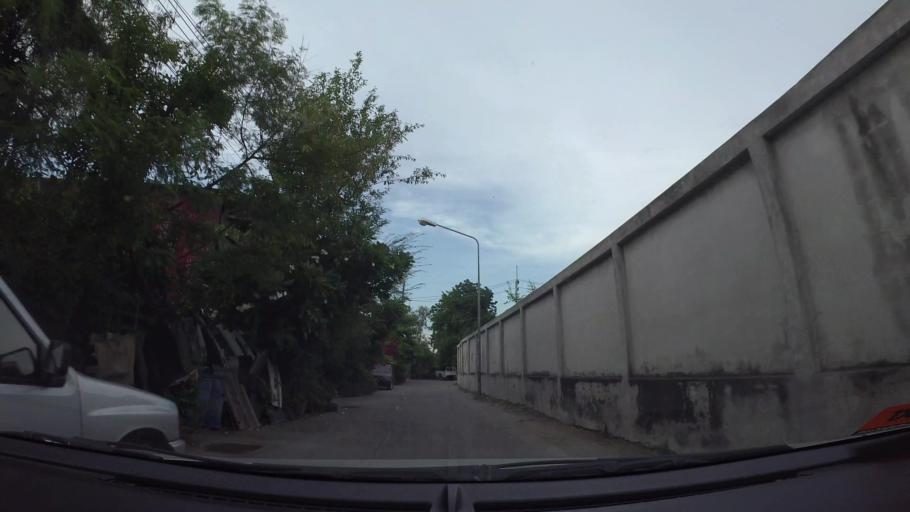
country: TH
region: Chon Buri
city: Chon Buri
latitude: 13.3354
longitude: 100.9816
